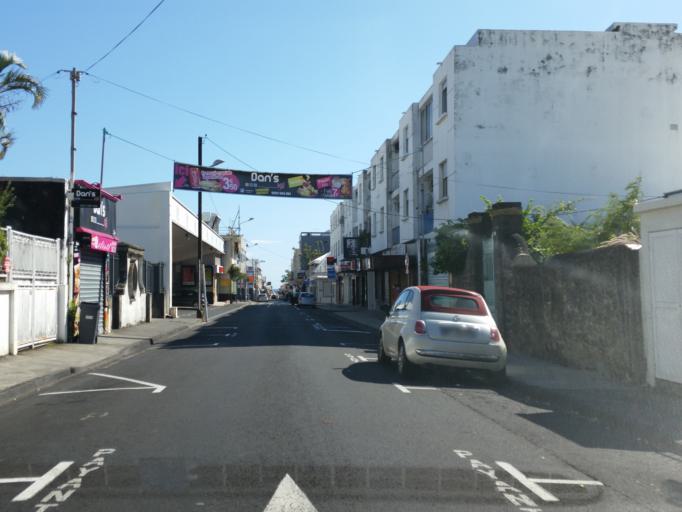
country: RE
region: Reunion
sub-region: Reunion
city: Saint-Denis
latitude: -20.8826
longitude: 55.4513
